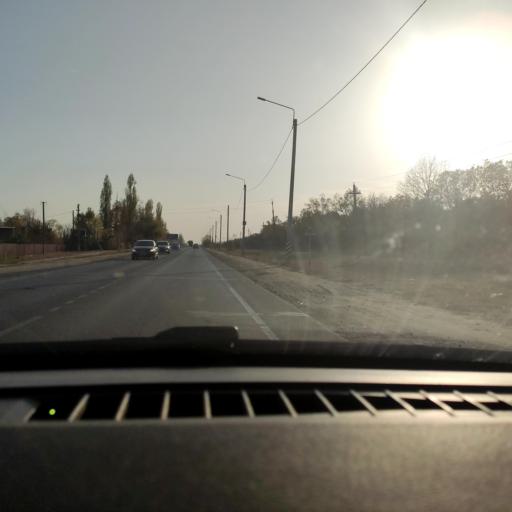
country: RU
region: Voronezj
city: Semiluki
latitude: 51.7314
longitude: 39.0396
